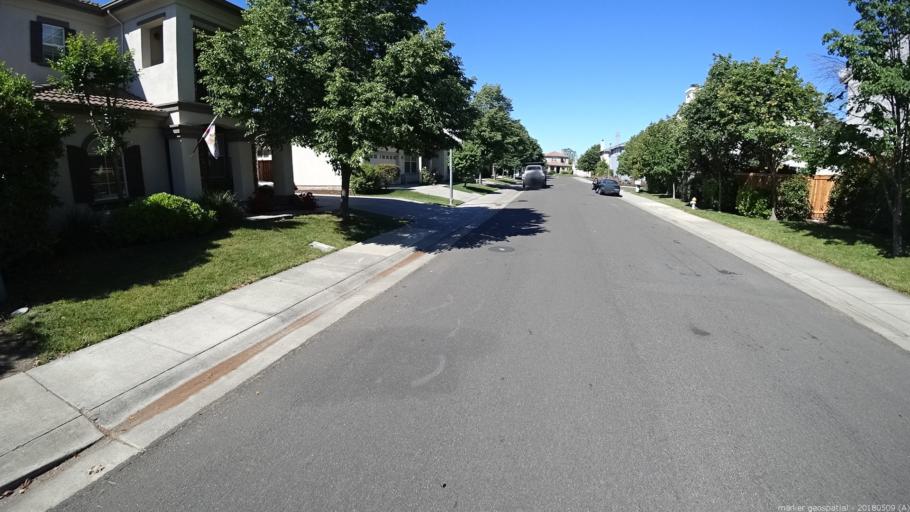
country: US
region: California
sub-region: Sacramento County
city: Elverta
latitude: 38.6715
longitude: -121.5211
